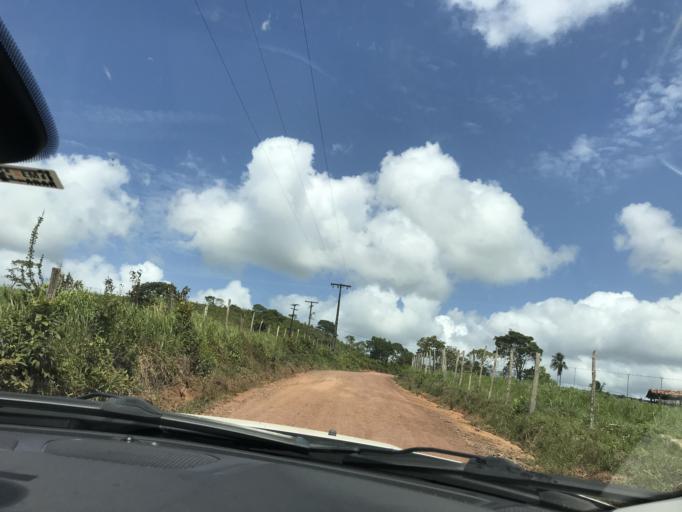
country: BR
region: Bahia
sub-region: Entre Rios
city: Entre Rios
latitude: -12.1832
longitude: -38.0572
